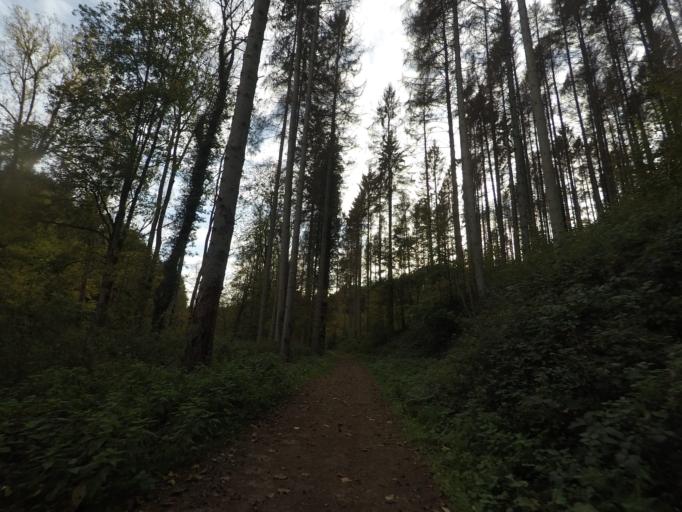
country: LU
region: Luxembourg
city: Itzig
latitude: 49.6005
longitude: 6.1616
